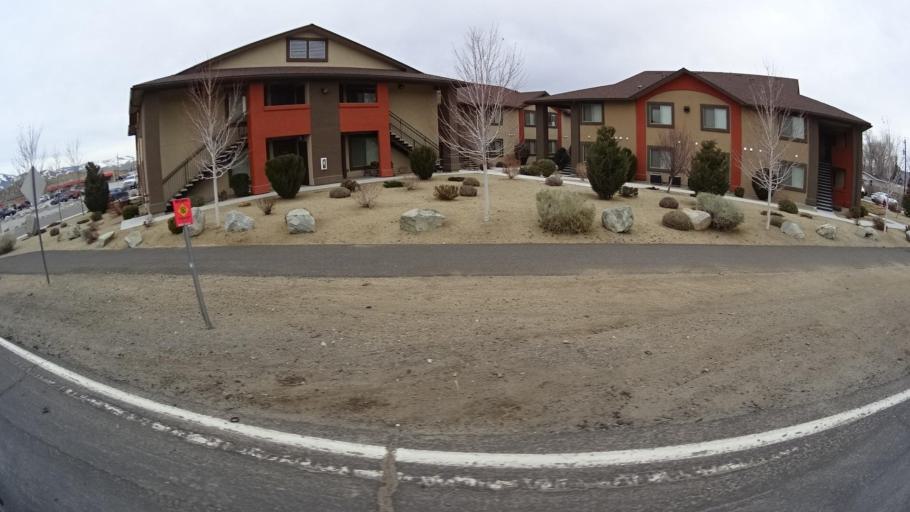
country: US
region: Nevada
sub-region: Washoe County
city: Lemmon Valley
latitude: 39.6389
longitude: -119.8419
